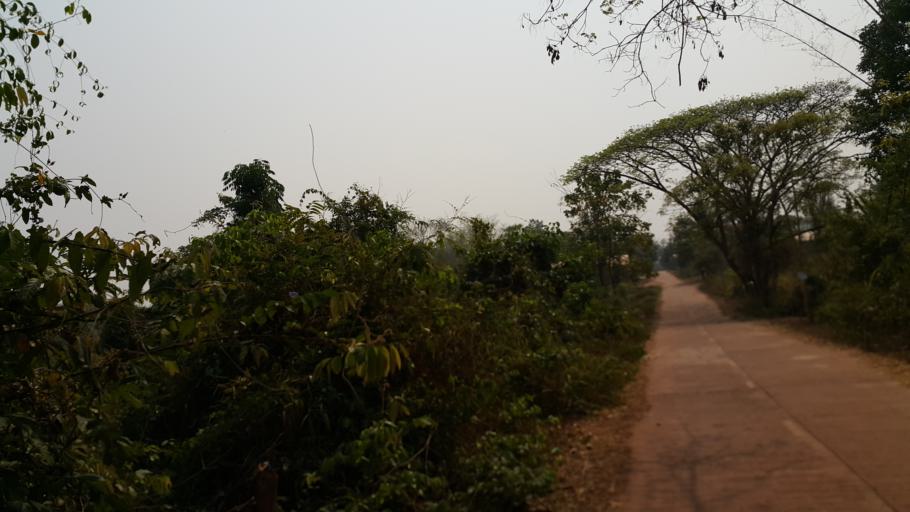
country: TH
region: Nakhon Phanom
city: Ban Phaeng
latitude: 17.8328
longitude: 104.2607
